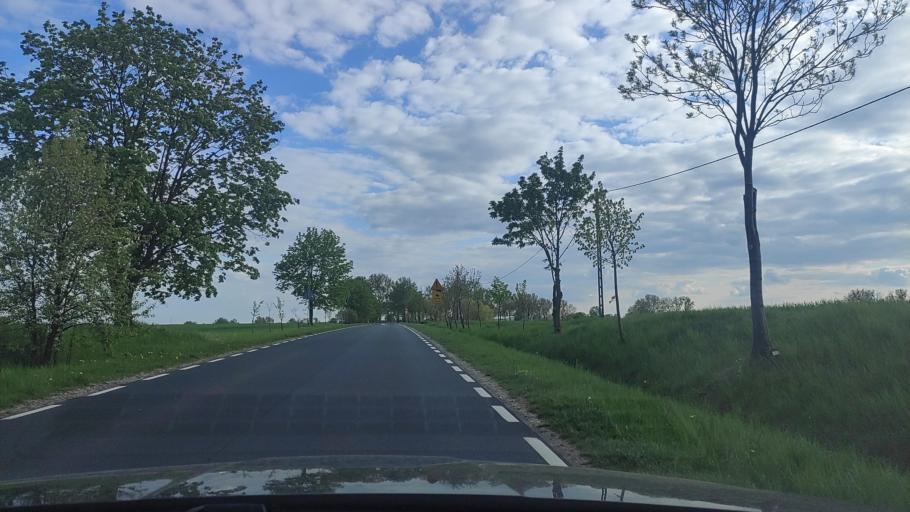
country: PL
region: Greater Poland Voivodeship
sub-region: Powiat poznanski
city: Kostrzyn
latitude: 52.4421
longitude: 17.2422
